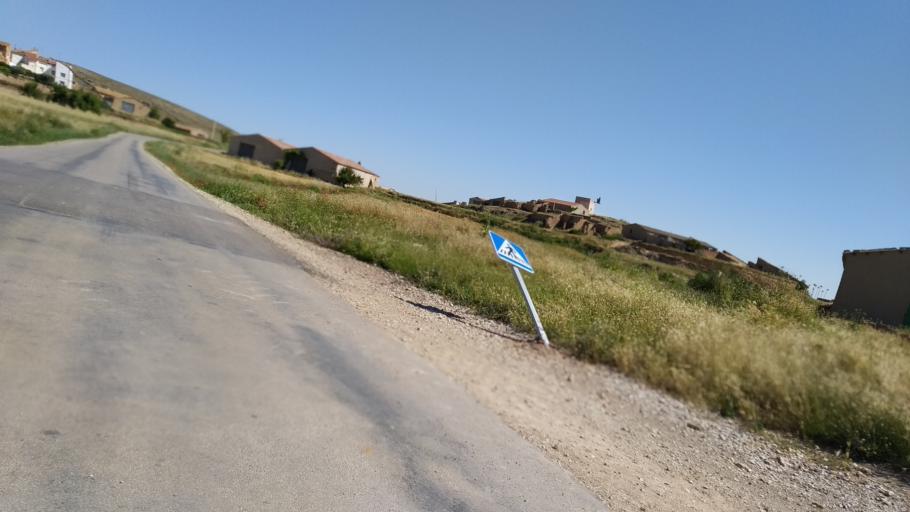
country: ES
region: Aragon
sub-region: Provincia de Teruel
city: Monforte de Moyuela
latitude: 41.0521
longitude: -1.0125
